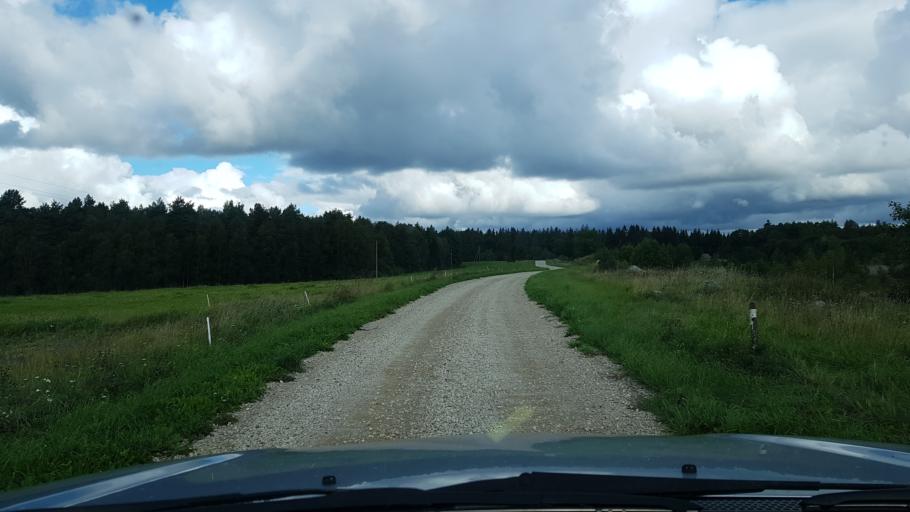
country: EE
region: Harju
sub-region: Raasiku vald
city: Arukula
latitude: 59.2871
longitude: 25.0999
